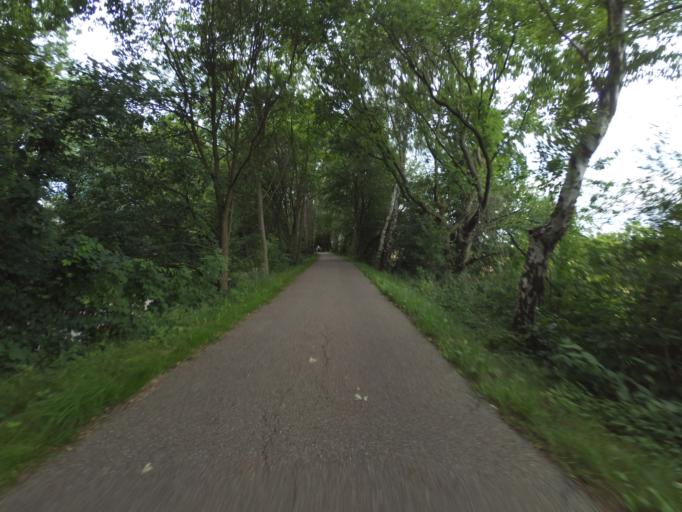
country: DE
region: North Rhine-Westphalia
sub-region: Regierungsbezirk Koln
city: Wurselen
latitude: 50.7671
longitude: 6.1655
